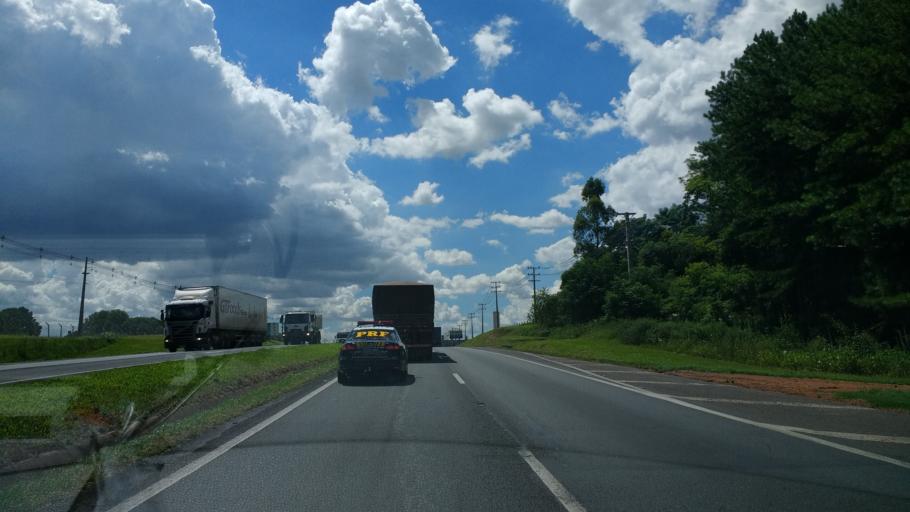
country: BR
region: Parana
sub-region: Ponta Grossa
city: Ponta Grossa
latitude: -25.1959
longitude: -50.0762
